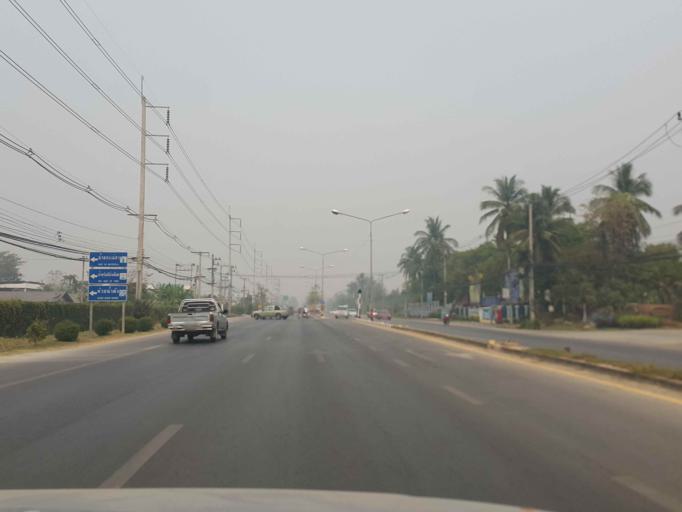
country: TH
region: Chiang Mai
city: San Sai
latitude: 18.9178
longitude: 98.9966
